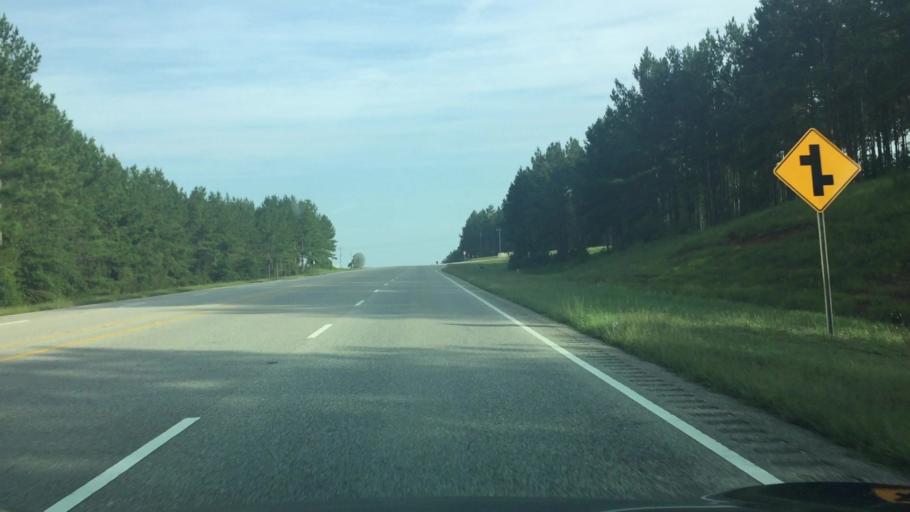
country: US
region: Alabama
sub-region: Butler County
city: Georgiana
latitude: 31.4806
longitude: -86.6759
